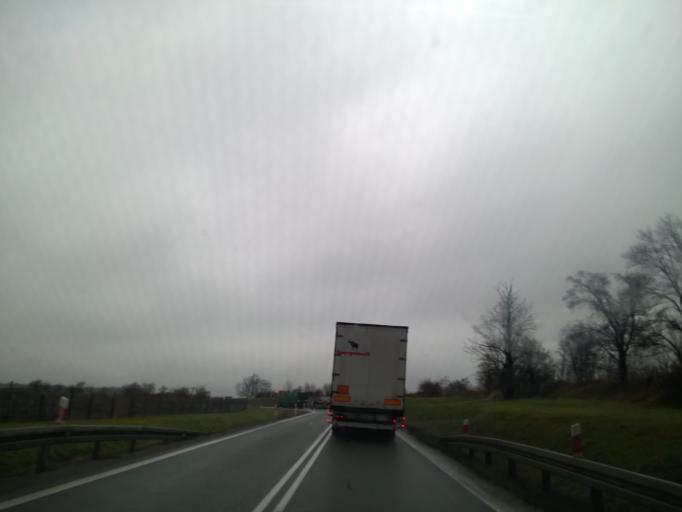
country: PL
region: Lower Silesian Voivodeship
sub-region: Powiat wroclawski
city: Tyniec Maly
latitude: 51.0385
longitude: 16.8936
